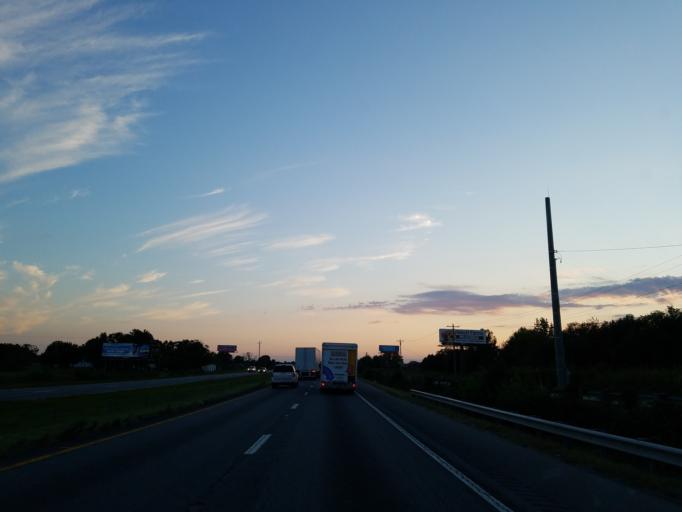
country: US
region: South Carolina
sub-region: Spartanburg County
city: Cowpens
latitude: 35.0666
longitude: -81.7695
